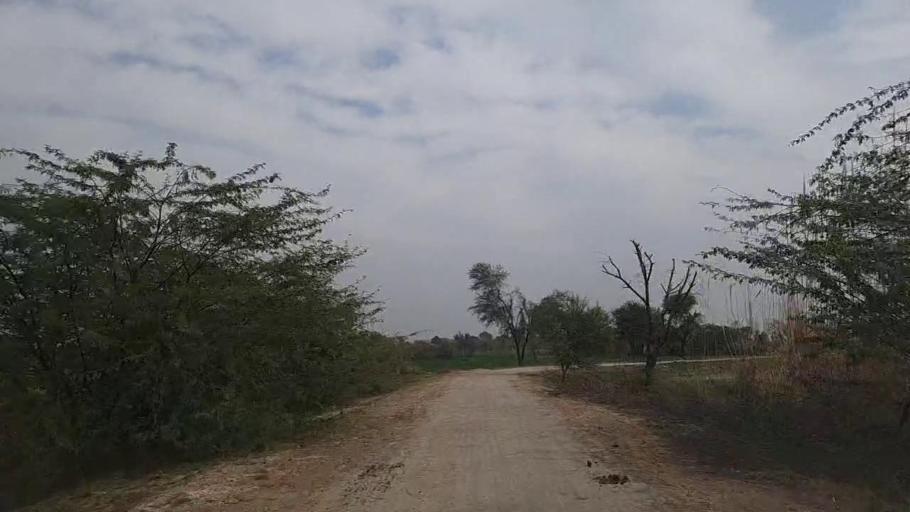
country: PK
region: Sindh
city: Daur
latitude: 26.4331
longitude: 68.4659
